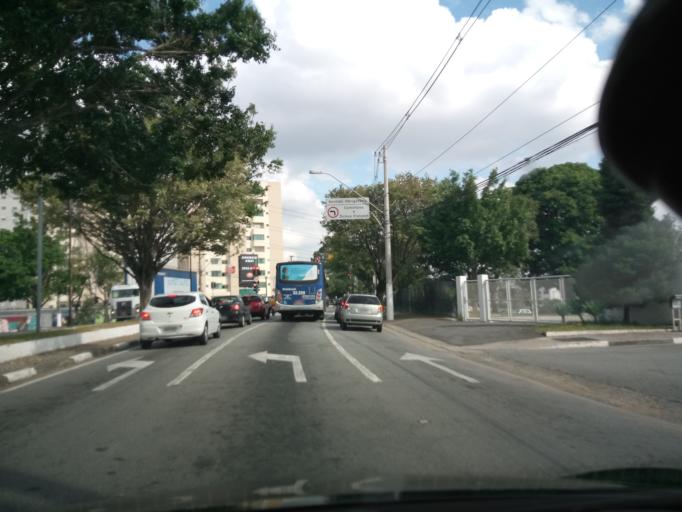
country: BR
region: Sao Paulo
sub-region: Sao Bernardo Do Campo
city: Sao Bernardo do Campo
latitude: -23.6709
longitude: -46.5676
